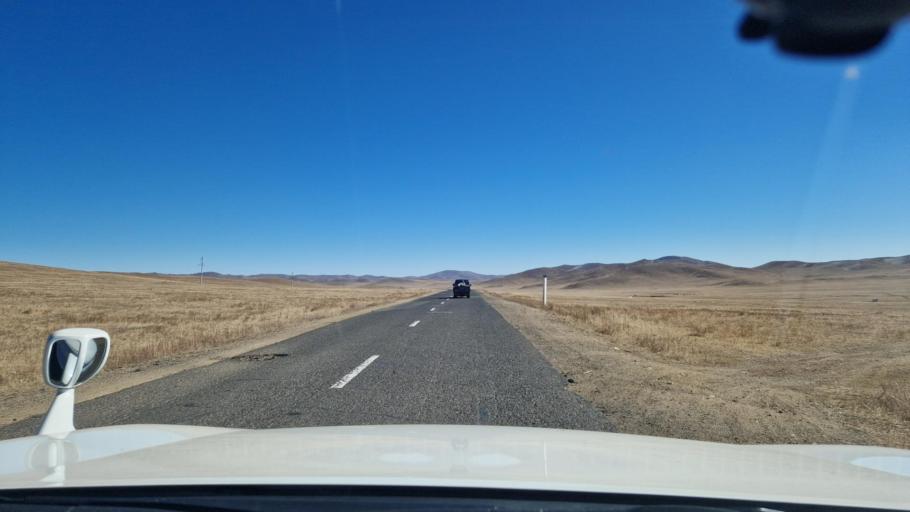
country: MN
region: Hentiy
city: Modot
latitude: 47.7695
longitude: 108.8731
